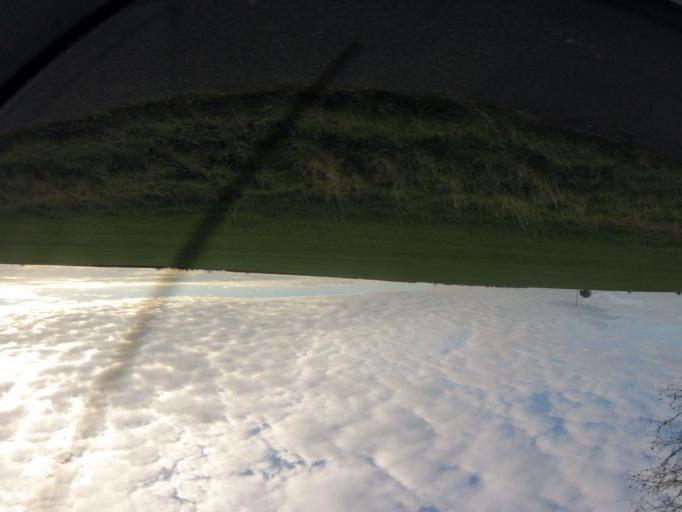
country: DE
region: Thuringia
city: Vollmershain
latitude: 50.8588
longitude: 12.2992
